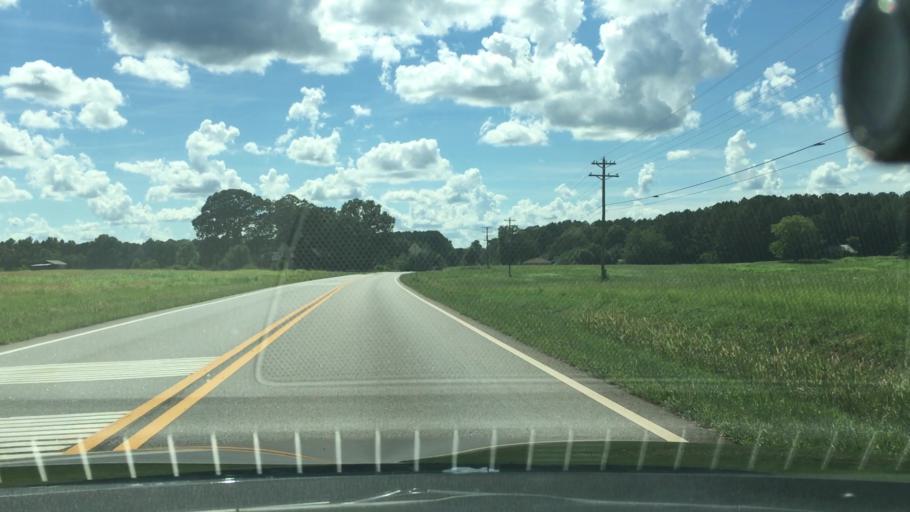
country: US
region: Georgia
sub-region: Butts County
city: Indian Springs
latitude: 33.2882
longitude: -83.8971
